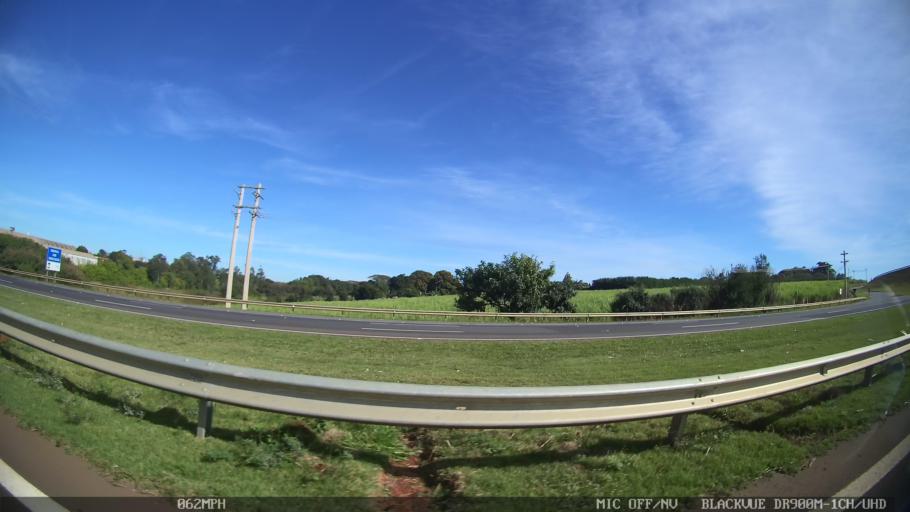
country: BR
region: Sao Paulo
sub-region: Araras
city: Araras
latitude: -22.3803
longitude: -47.3943
